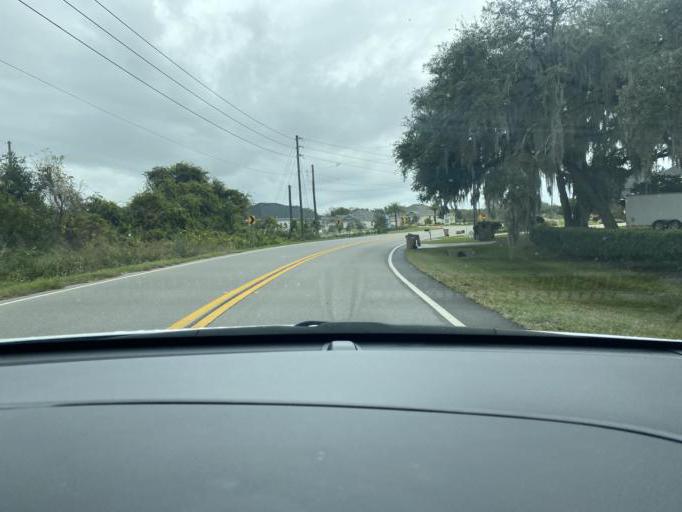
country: US
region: Florida
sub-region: Lake County
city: Clermont
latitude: 28.5828
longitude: -81.7863
